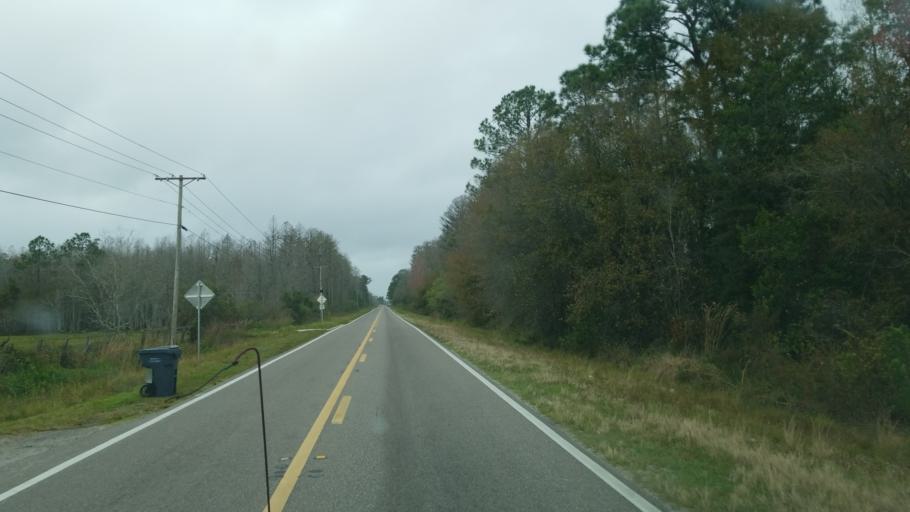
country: US
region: Florida
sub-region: Polk County
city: Polk City
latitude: 28.2585
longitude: -81.8279
